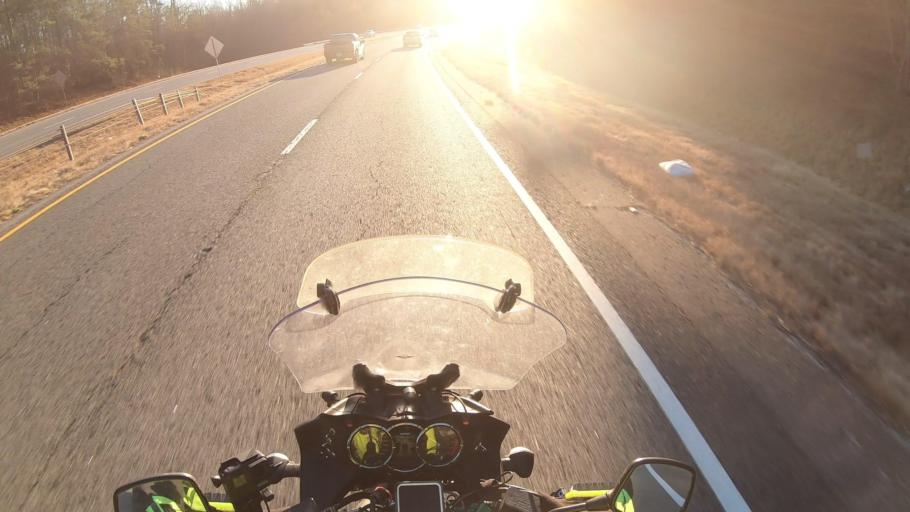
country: US
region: Georgia
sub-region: Lumpkin County
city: Dahlonega
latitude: 34.4505
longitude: -83.9795
